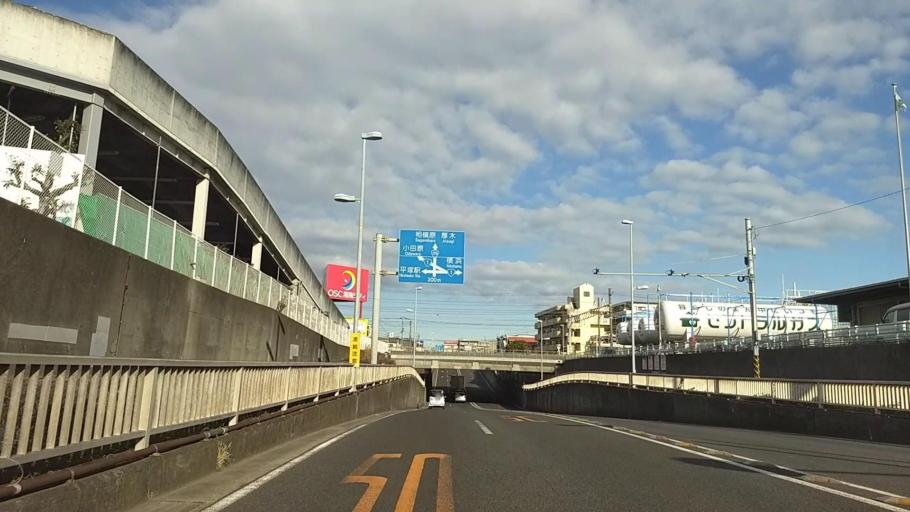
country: JP
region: Kanagawa
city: Hiratsuka
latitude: 35.3285
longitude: 139.3598
